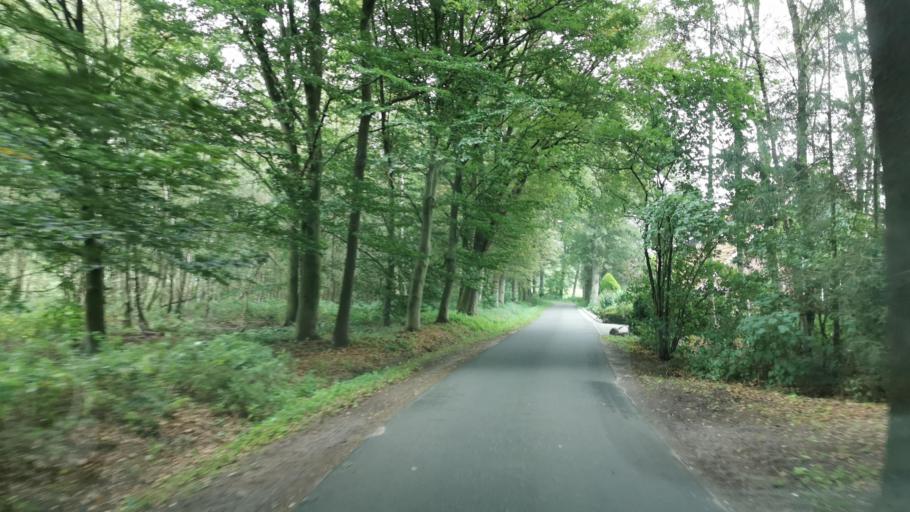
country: NL
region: Overijssel
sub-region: Gemeente Oldenzaal
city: Oldenzaal
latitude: 52.3015
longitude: 6.9685
